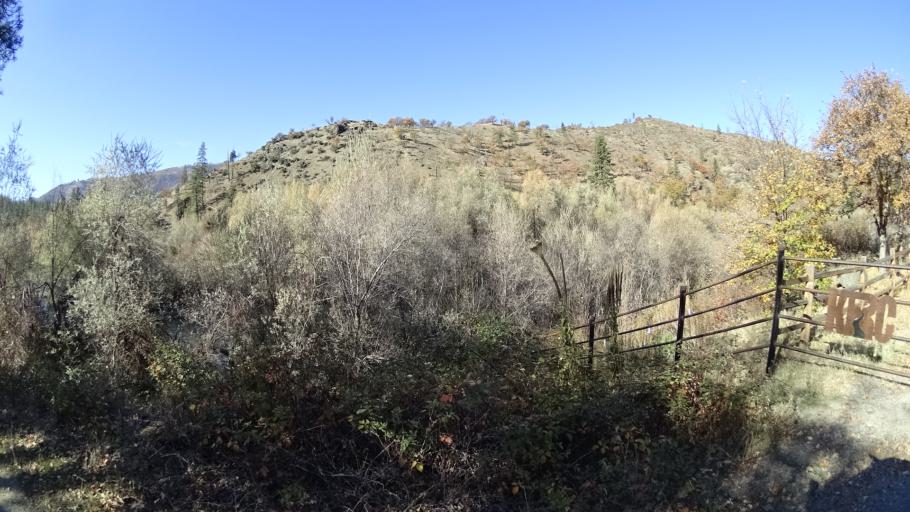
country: US
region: California
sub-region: Siskiyou County
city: Yreka
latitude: 41.8635
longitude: -122.8180
